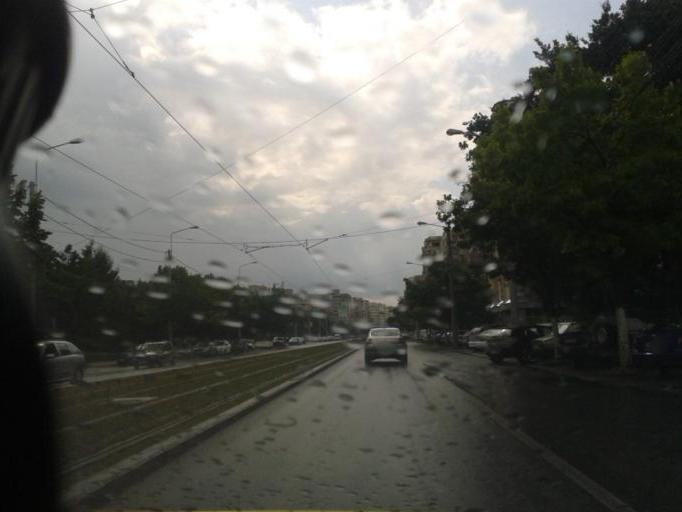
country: RO
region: Prahova
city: Ploiesti
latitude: 44.9467
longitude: 26.0153
